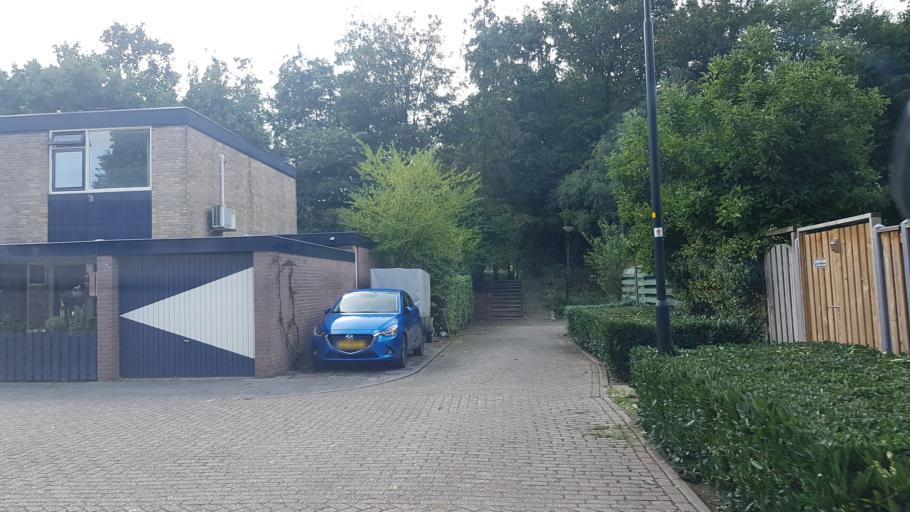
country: NL
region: Gelderland
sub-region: Gemeente Apeldoorn
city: Beekbergen
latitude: 52.1874
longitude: 5.9335
